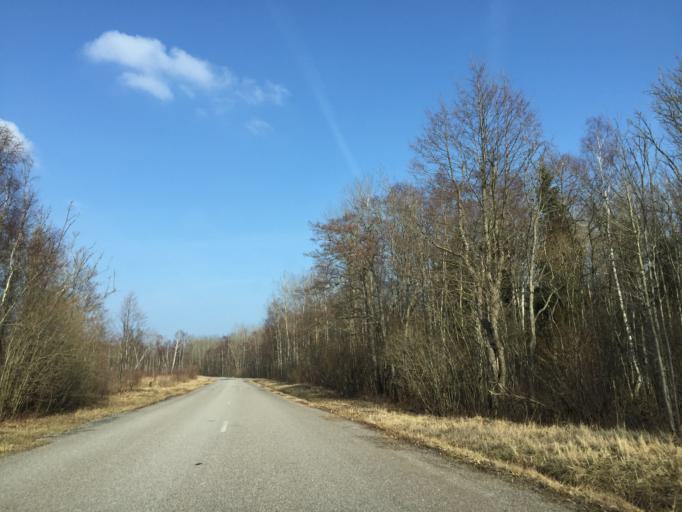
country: EE
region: Saare
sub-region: Kuressaare linn
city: Kuressaare
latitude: 58.0520
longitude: 22.1338
